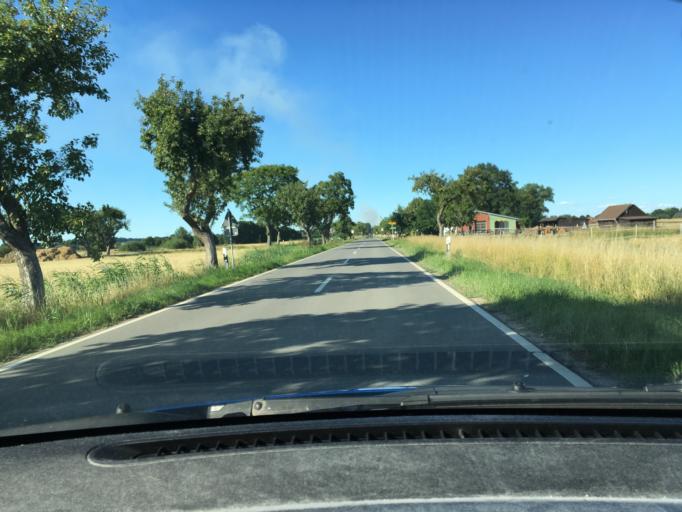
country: DE
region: Mecklenburg-Vorpommern
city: Boizenburg
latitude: 53.3467
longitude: 10.6980
